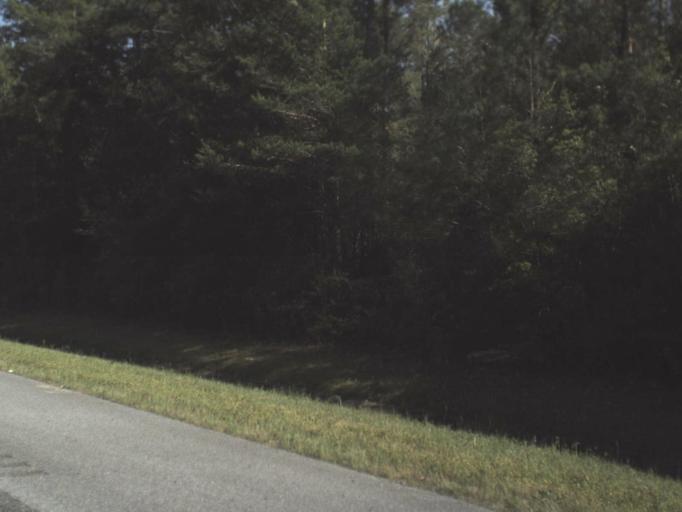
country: US
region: Florida
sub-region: Okaloosa County
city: Crestview
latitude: 30.7134
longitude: -86.6281
